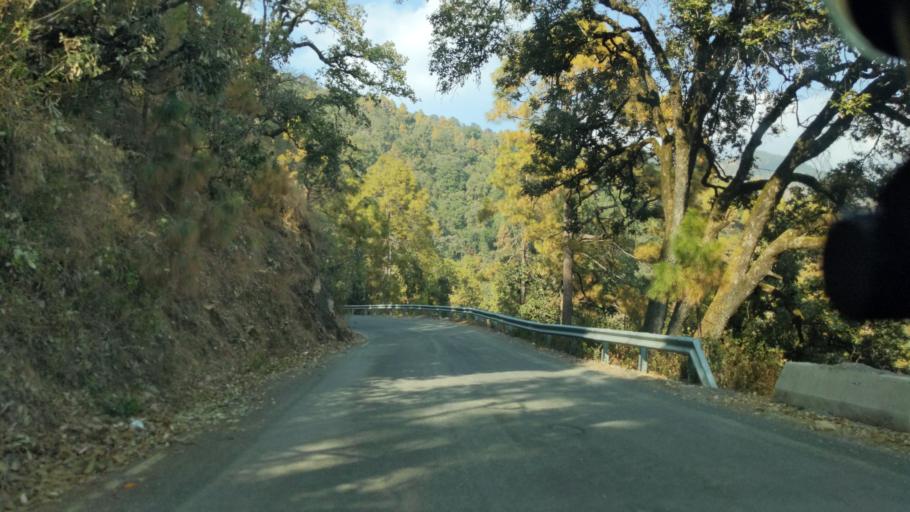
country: IN
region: Uttarakhand
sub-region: Naini Tal
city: Bhowali
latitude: 29.4000
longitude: 79.5352
